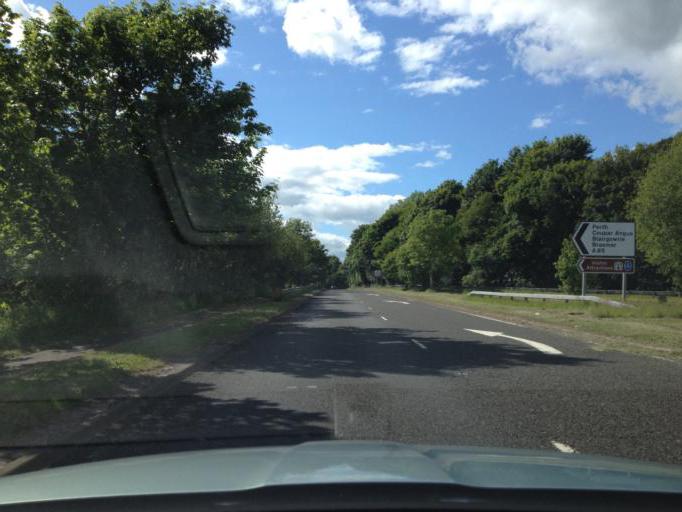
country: GB
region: Scotland
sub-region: Perth and Kinross
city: Perth
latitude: 56.3816
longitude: -3.4108
